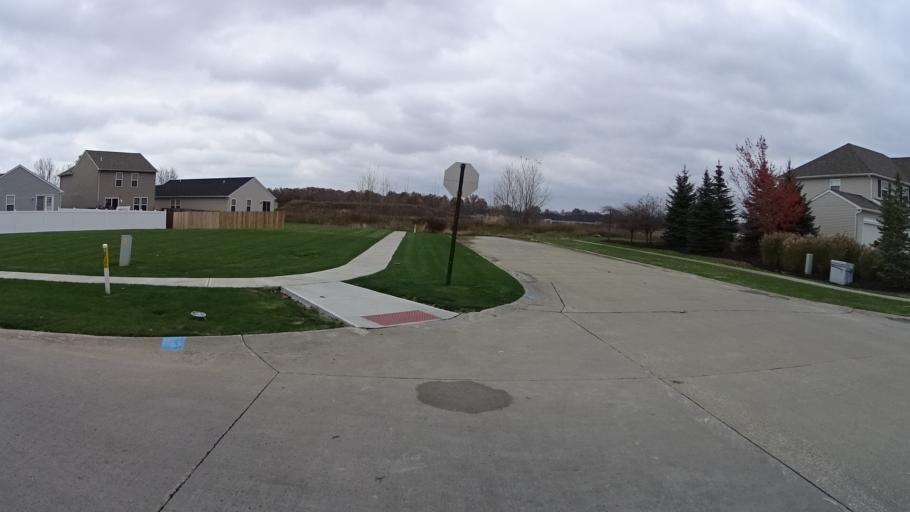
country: US
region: Ohio
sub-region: Lorain County
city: Amherst
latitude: 41.4316
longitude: -82.2205
